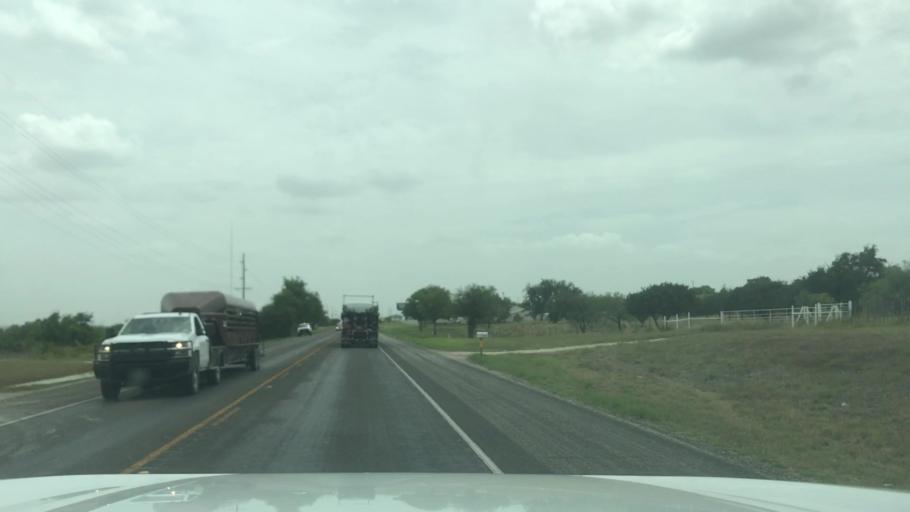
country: US
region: Texas
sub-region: Bosque County
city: Clifton
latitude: 31.7625
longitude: -97.5646
